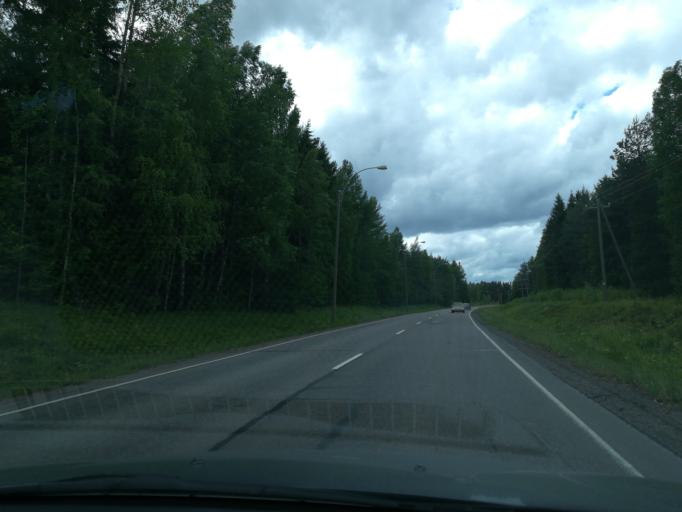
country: FI
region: South Karelia
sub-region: Lappeenranta
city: Lappeenranta
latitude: 61.0512
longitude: 28.3309
